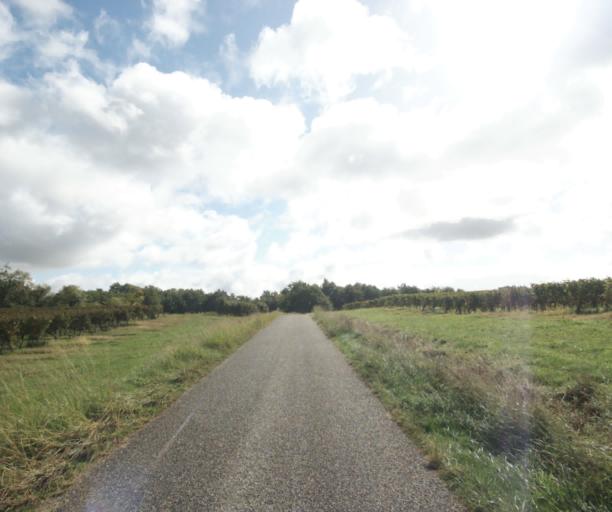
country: FR
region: Midi-Pyrenees
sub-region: Departement du Gers
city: Le Houga
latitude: 43.8317
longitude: -0.0986
